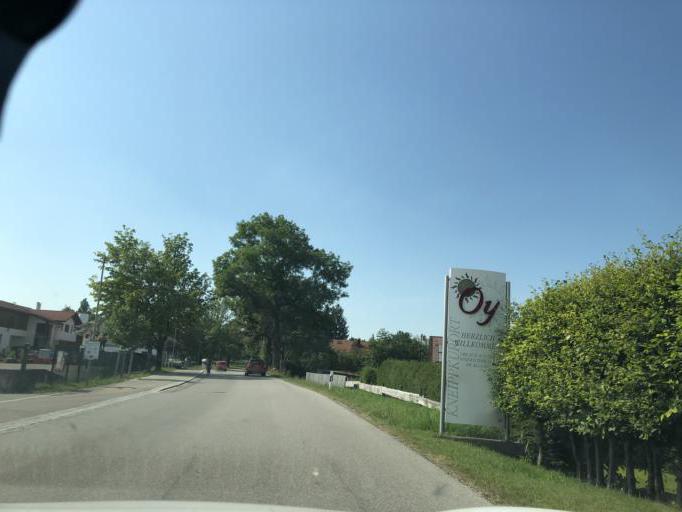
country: DE
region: Bavaria
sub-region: Swabia
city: Oy-Mittelberg
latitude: 47.6416
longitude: 10.4573
